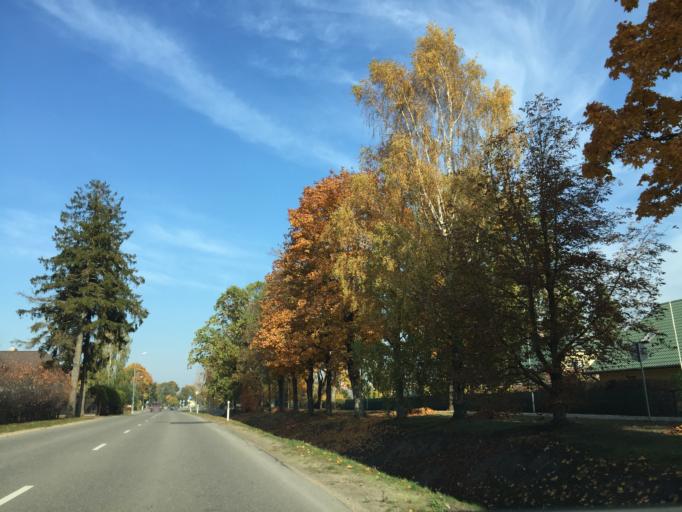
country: LV
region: Marupe
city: Marupe
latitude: 56.8934
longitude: 24.0460
